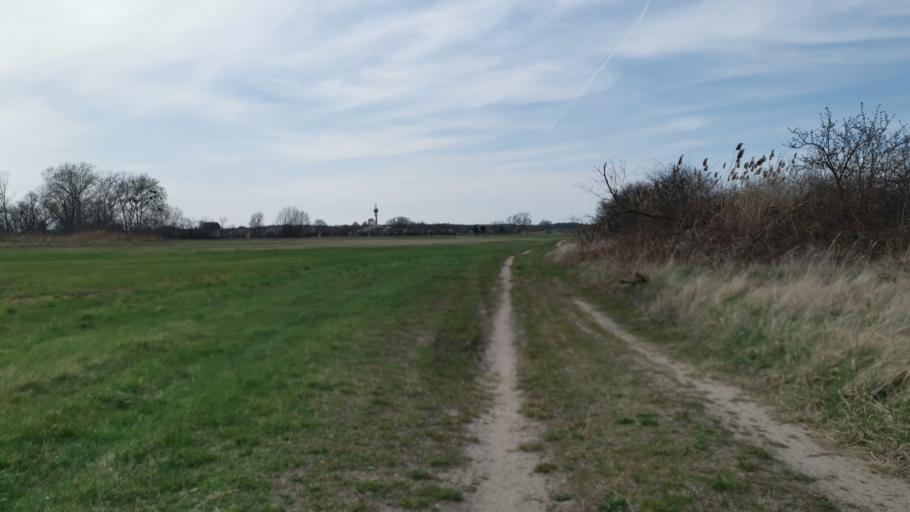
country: CZ
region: South Moravian
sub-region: Okres Breclav
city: Lanzhot
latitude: 48.6958
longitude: 17.0274
